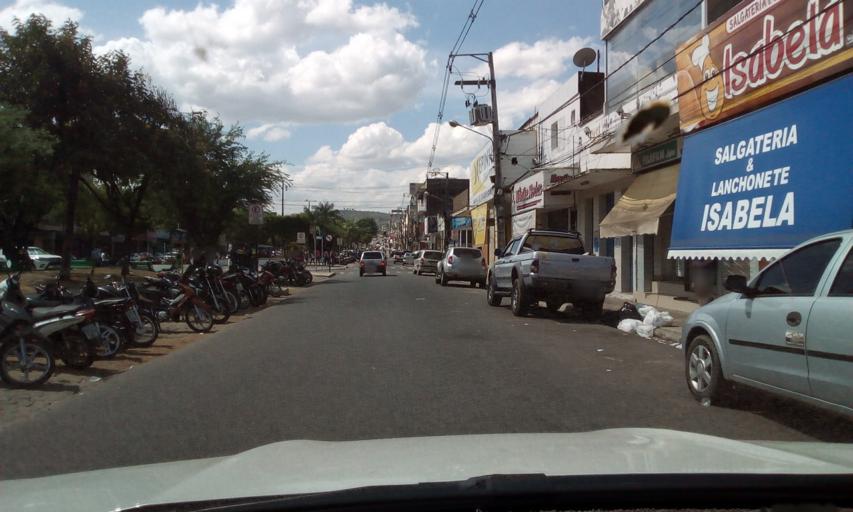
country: BR
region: Paraiba
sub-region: Guarabira
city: Guarabira
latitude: -6.8531
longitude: -35.4902
